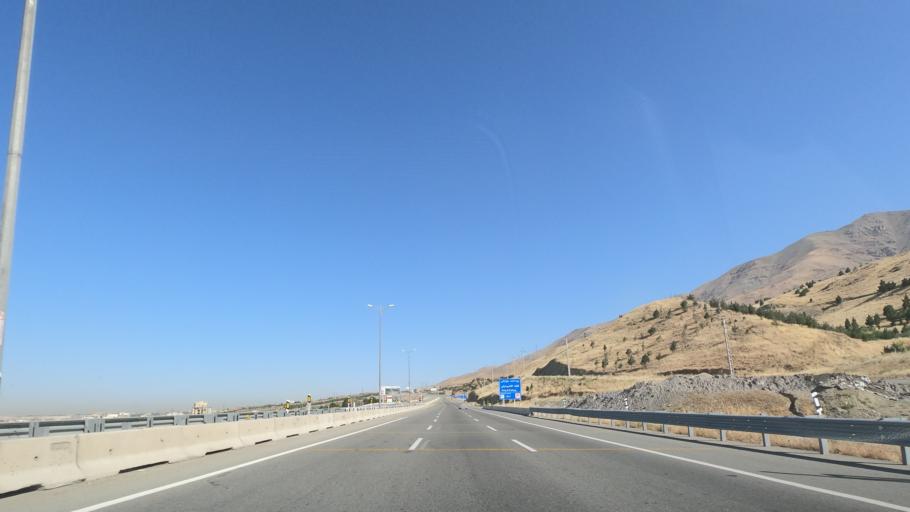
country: IR
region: Tehran
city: Shahr-e Qods
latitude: 35.7557
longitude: 51.0806
